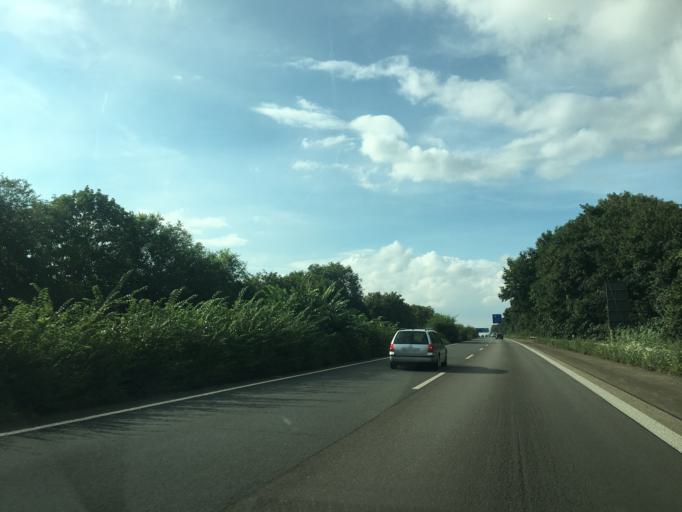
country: DE
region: North Rhine-Westphalia
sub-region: Regierungsbezirk Dusseldorf
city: Krefeld
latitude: 51.3280
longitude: 6.6296
